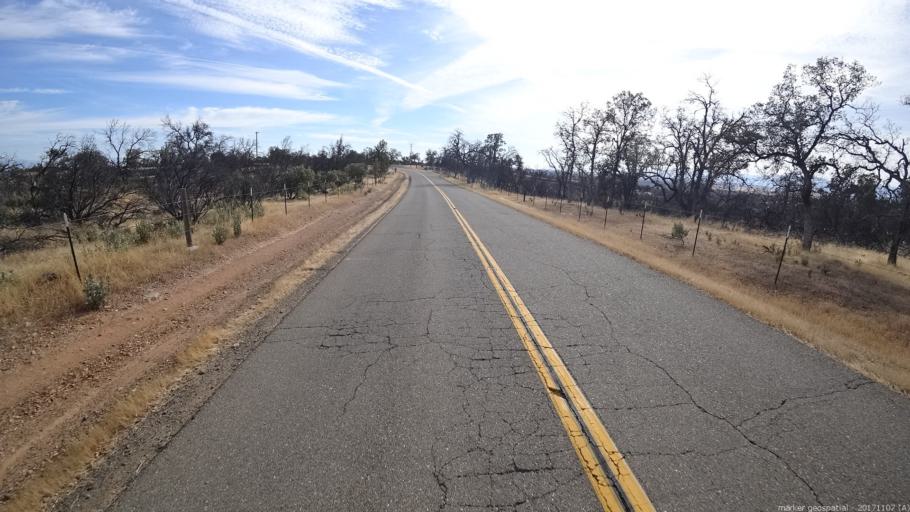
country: US
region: California
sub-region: Shasta County
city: Shasta
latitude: 40.4713
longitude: -122.5447
